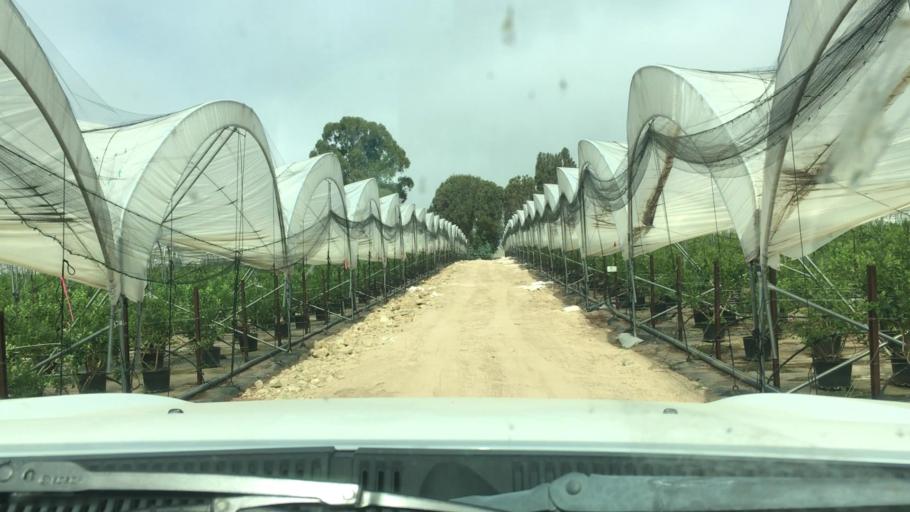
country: US
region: California
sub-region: San Luis Obispo County
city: Callender
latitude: 35.0637
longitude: -120.5698
